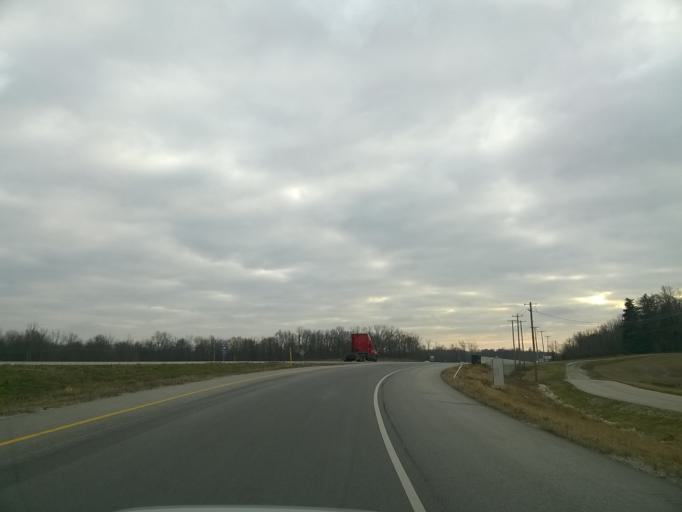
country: US
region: Indiana
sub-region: Hamilton County
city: Westfield
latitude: 40.0901
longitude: -86.1281
